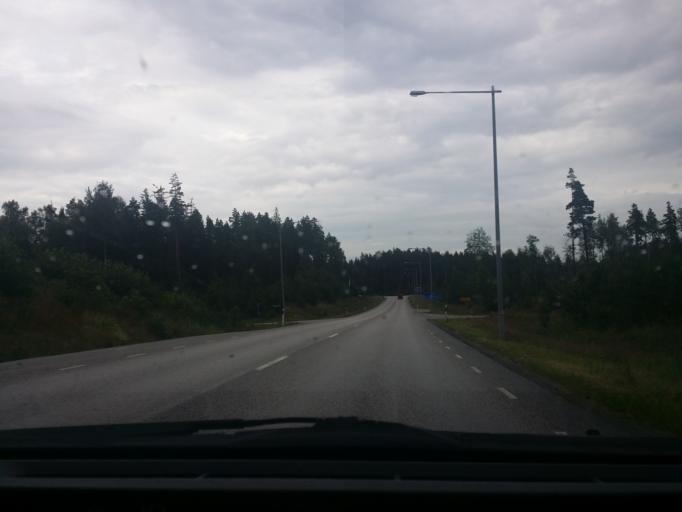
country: SE
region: OErebro
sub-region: Lindesbergs Kommun
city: Frovi
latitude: 59.4776
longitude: 15.3765
